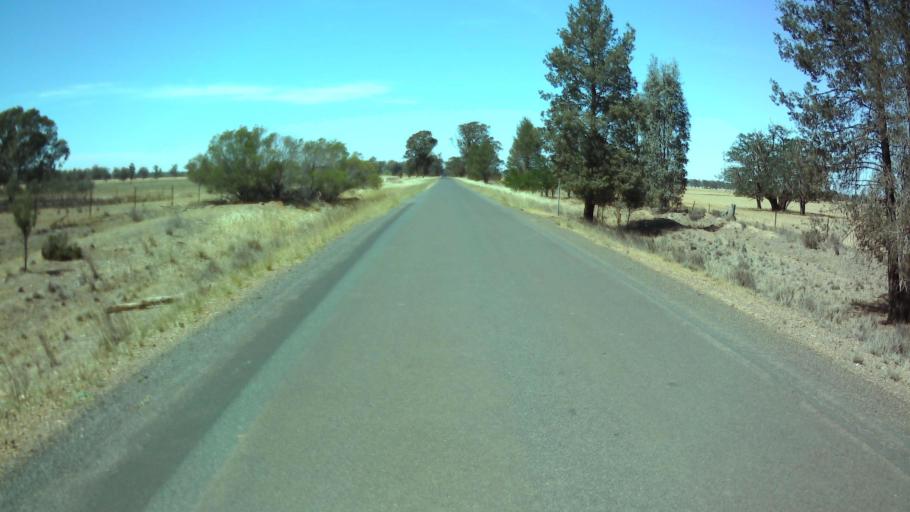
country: AU
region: New South Wales
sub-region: Weddin
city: Grenfell
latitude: -34.1031
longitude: 147.8873
